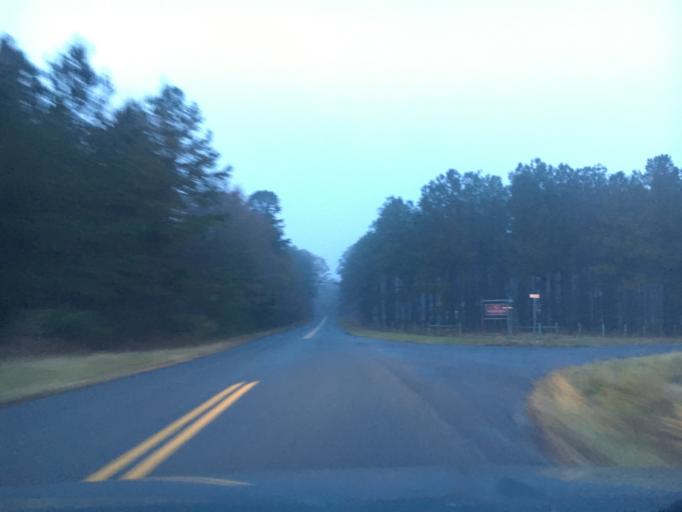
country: US
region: Virginia
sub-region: Halifax County
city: Mountain Road
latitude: 36.6831
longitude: -79.0322
